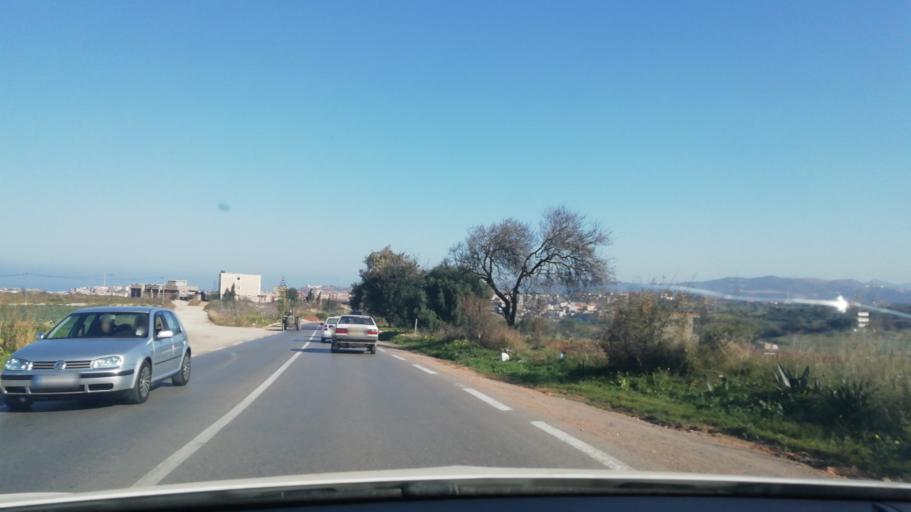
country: DZ
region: Tlemcen
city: Nedroma
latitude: 35.0775
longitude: -1.8783
